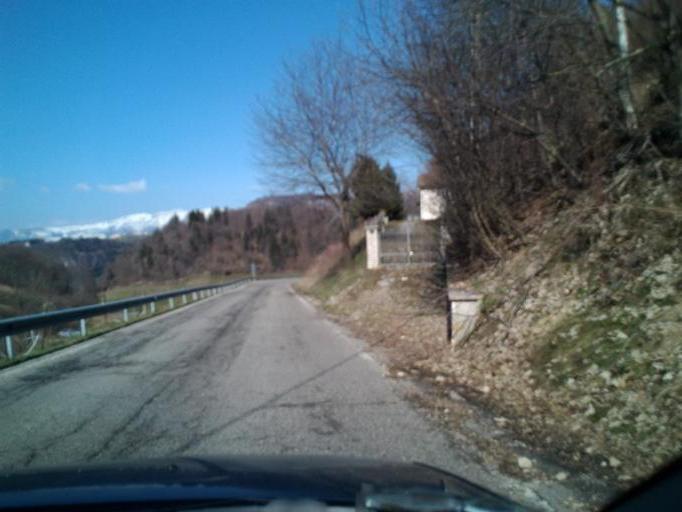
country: IT
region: Veneto
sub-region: Provincia di Verona
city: Bosco Chiesanuova
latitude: 45.6409
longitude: 11.0279
